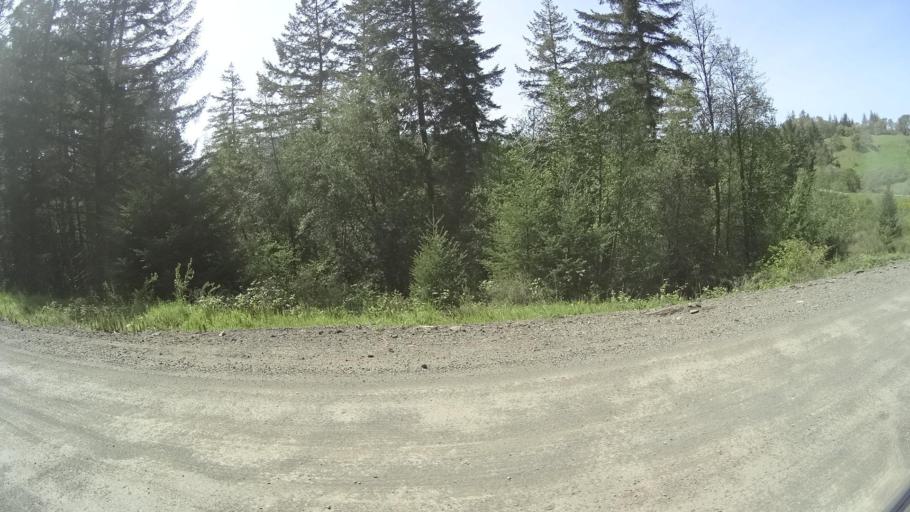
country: US
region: California
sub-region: Humboldt County
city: Redway
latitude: 40.4167
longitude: -123.7613
